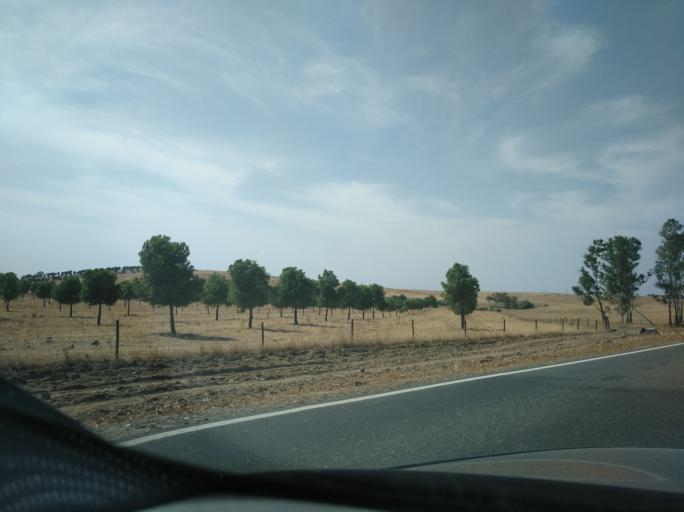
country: PT
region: Beja
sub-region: Mertola
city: Mertola
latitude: 37.7749
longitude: -7.8321
